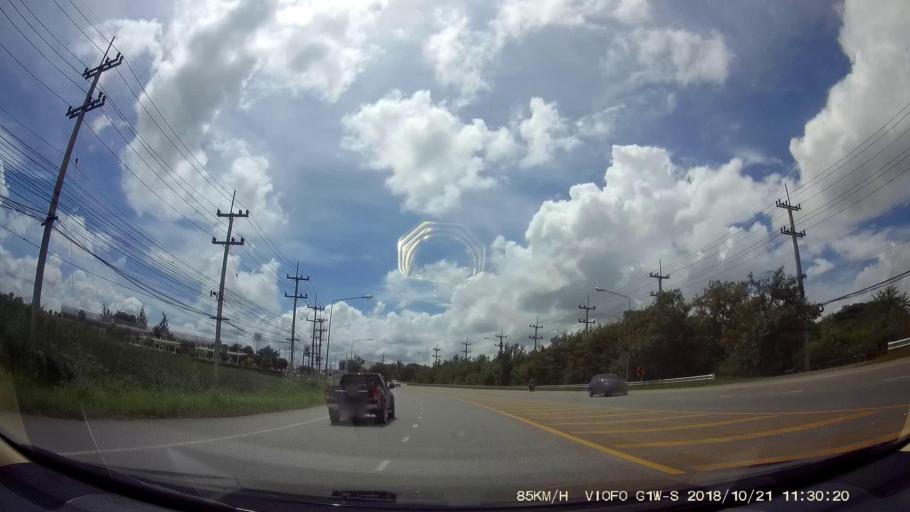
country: TH
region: Chaiyaphum
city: Chaiyaphum
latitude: 15.7798
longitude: 102.0253
